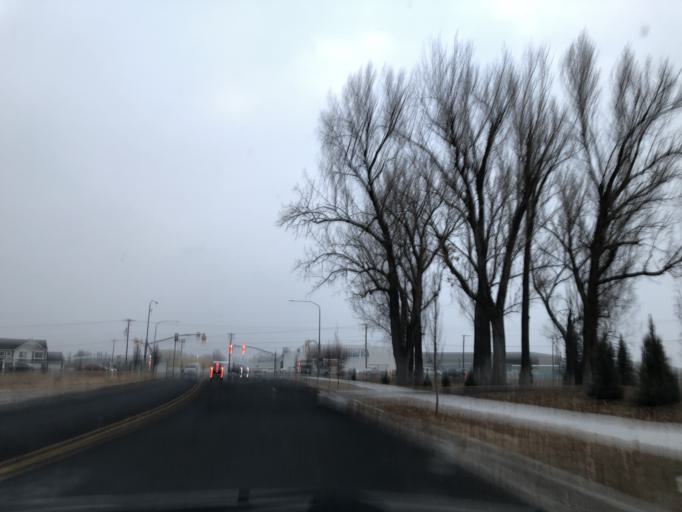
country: US
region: Utah
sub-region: Cache County
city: Providence
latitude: 41.7042
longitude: -111.8527
